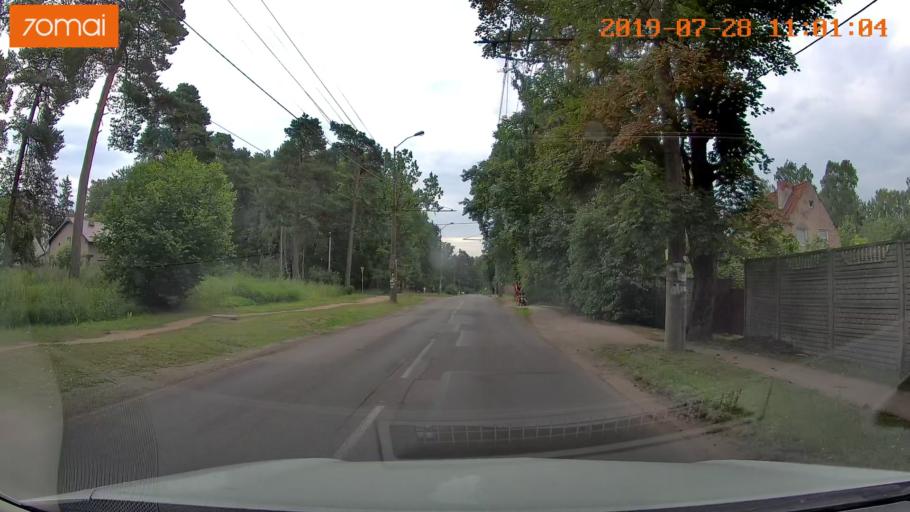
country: RU
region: Kaliningrad
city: Vzmorye
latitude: 54.7238
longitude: 20.3659
